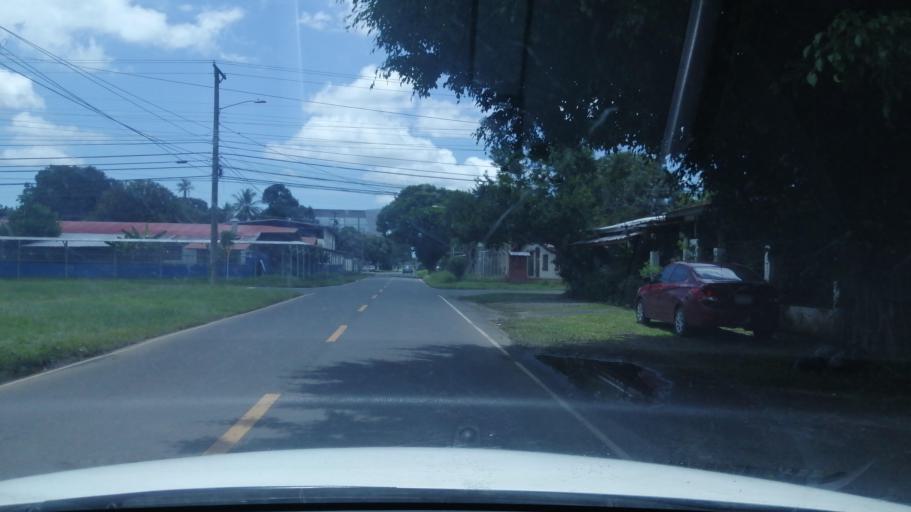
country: PA
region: Chiriqui
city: David
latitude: 8.4342
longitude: -82.4305
